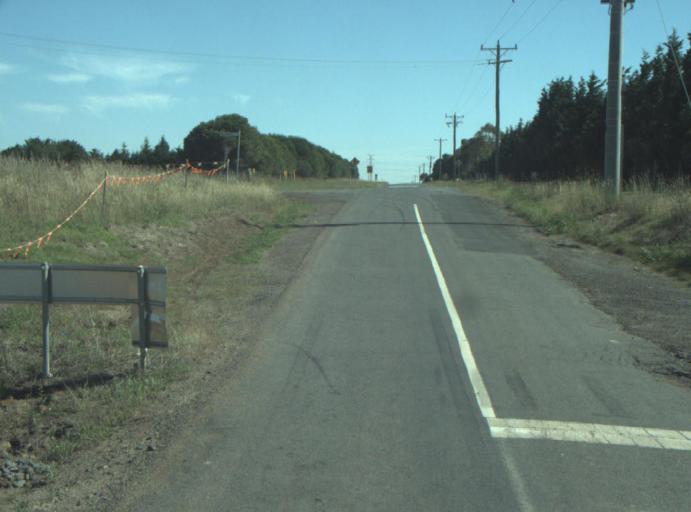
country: AU
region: Victoria
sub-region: Greater Geelong
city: Bell Post Hill
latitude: -38.0769
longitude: 144.3084
